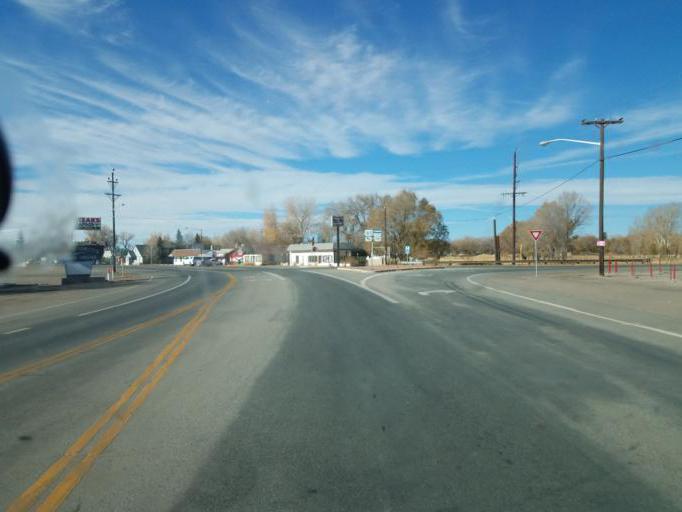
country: US
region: Colorado
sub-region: Alamosa County
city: Alamosa
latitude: 37.4732
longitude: -105.8567
